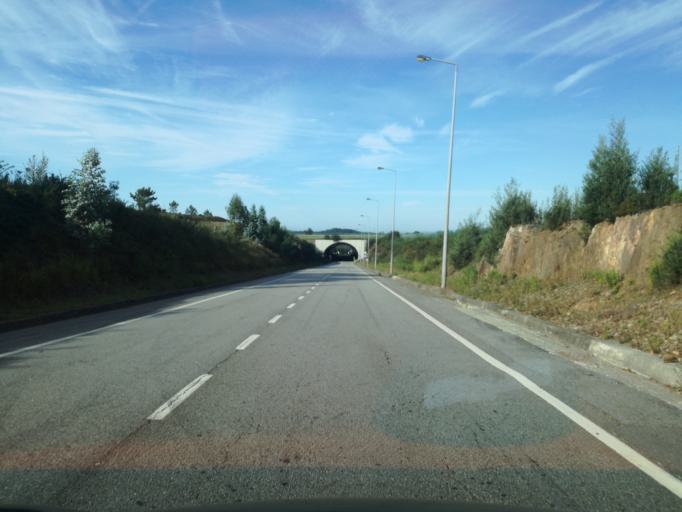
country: PT
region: Porto
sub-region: Trofa
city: Sao Romao do Coronado
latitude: 41.2845
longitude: -8.5174
